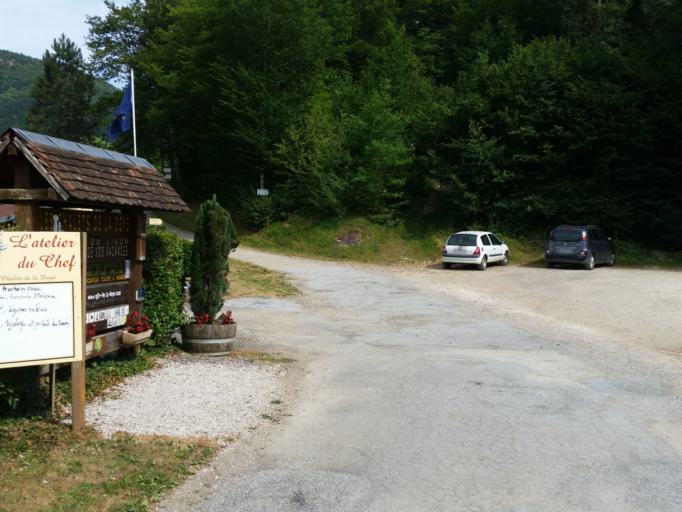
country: FR
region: Franche-Comte
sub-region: Departement du Jura
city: Salins-les-Bains
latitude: 46.9727
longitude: 5.9972
